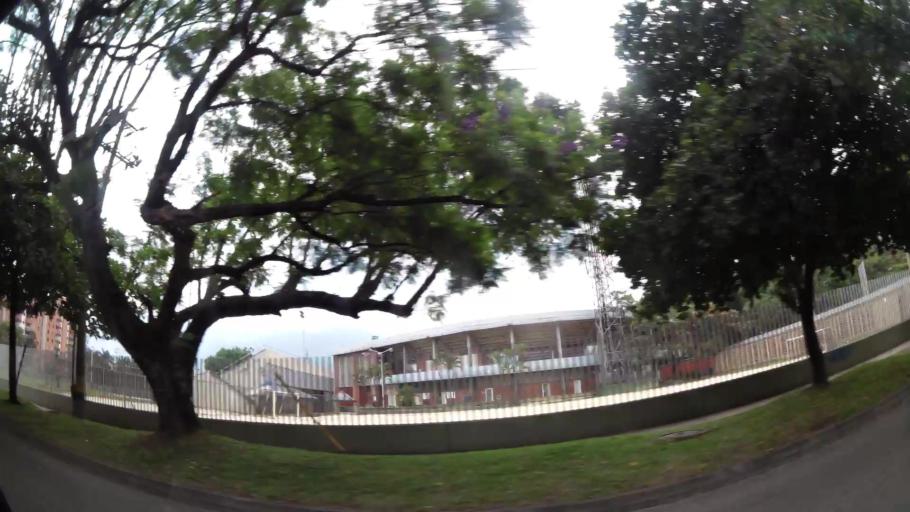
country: CO
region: Antioquia
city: Envigado
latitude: 6.1656
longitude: -75.5999
